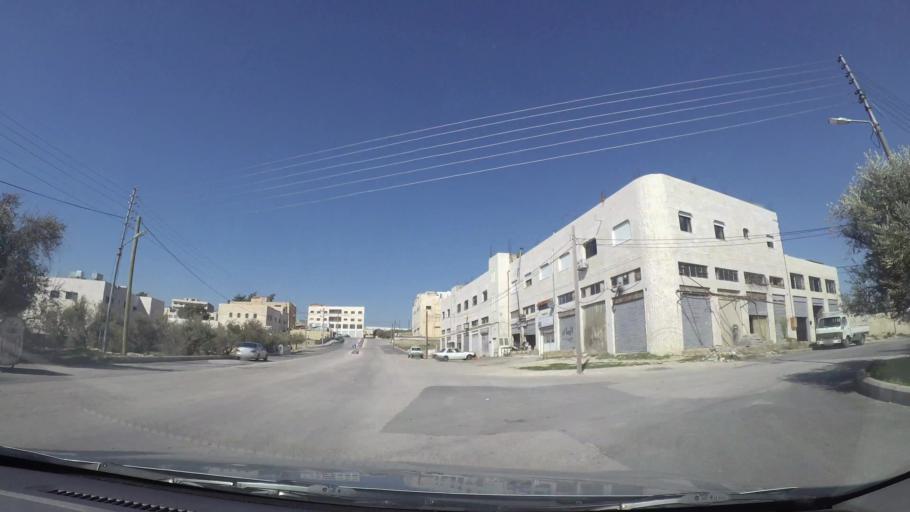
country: JO
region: Amman
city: Al Bunayyat ash Shamaliyah
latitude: 31.9067
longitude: 35.8974
